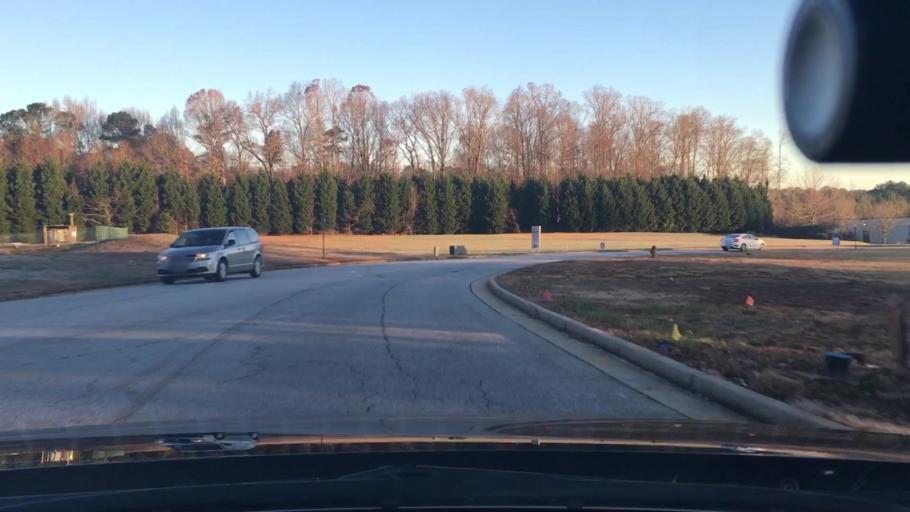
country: US
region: Georgia
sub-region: Fayette County
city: Peachtree City
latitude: 33.4107
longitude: -84.6855
